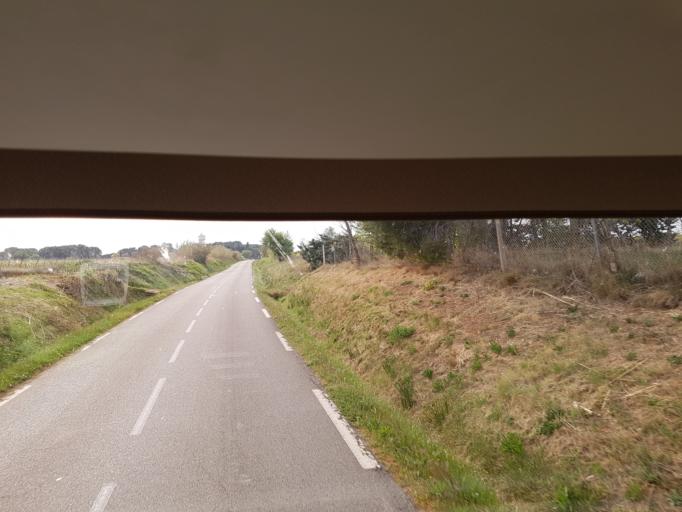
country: FR
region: Languedoc-Roussillon
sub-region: Departement de l'Herault
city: Marseillan
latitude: 43.3680
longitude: 3.5070
